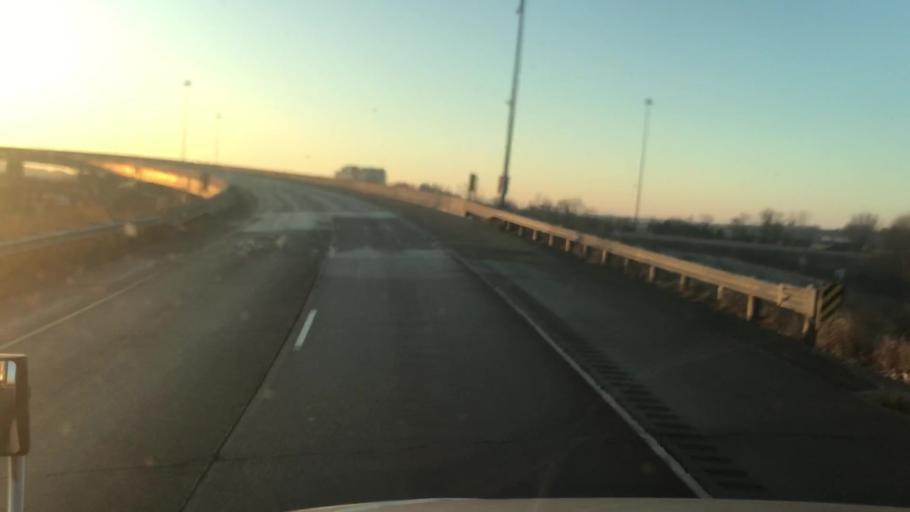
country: US
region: Iowa
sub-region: Black Hawk County
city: Evansdale
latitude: 42.4560
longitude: -92.3144
